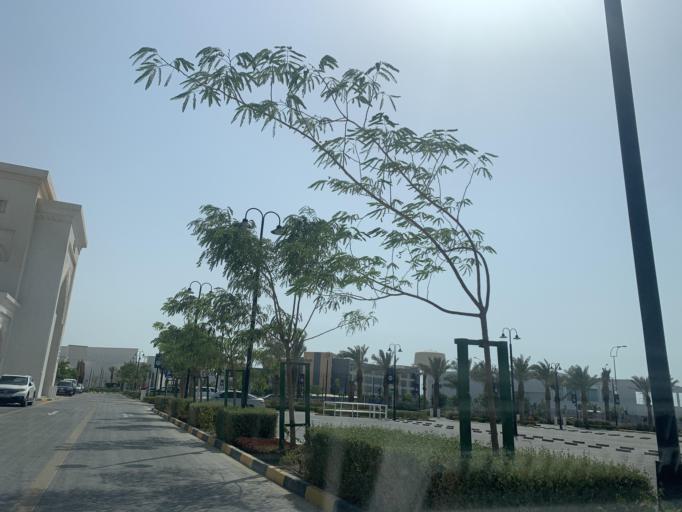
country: BH
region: Muharraq
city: Al Muharraq
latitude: 26.3054
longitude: 50.6370
